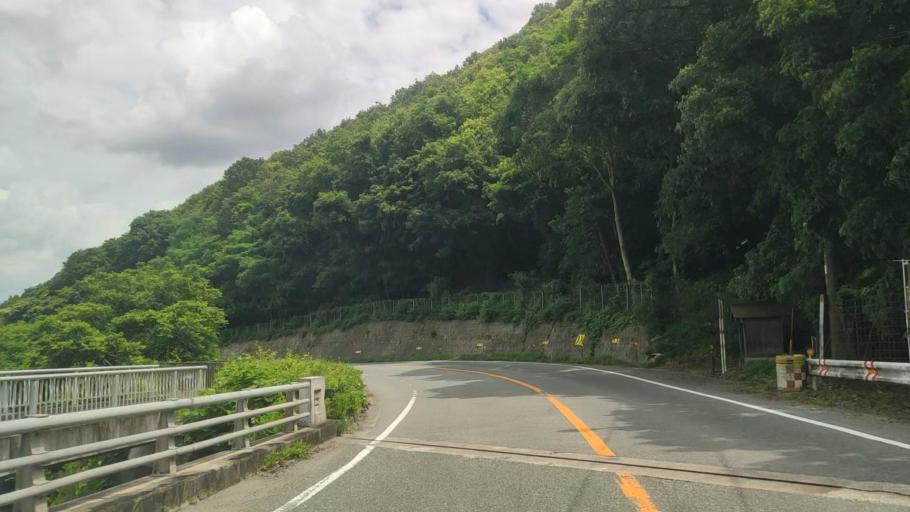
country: JP
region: Hyogo
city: Yamazakicho-nakabirose
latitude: 34.9406
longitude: 134.4962
